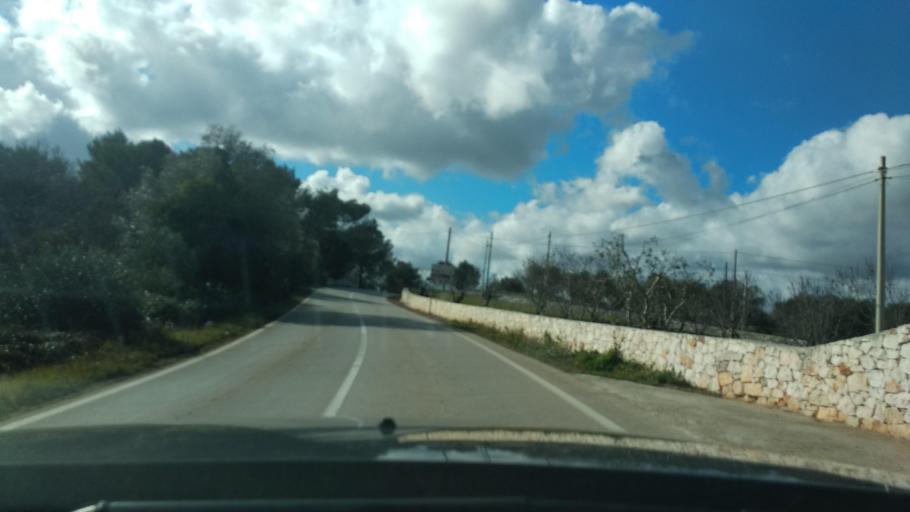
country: IT
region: Apulia
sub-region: Provincia di Brindisi
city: Casalini
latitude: 40.7050
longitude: 17.5032
